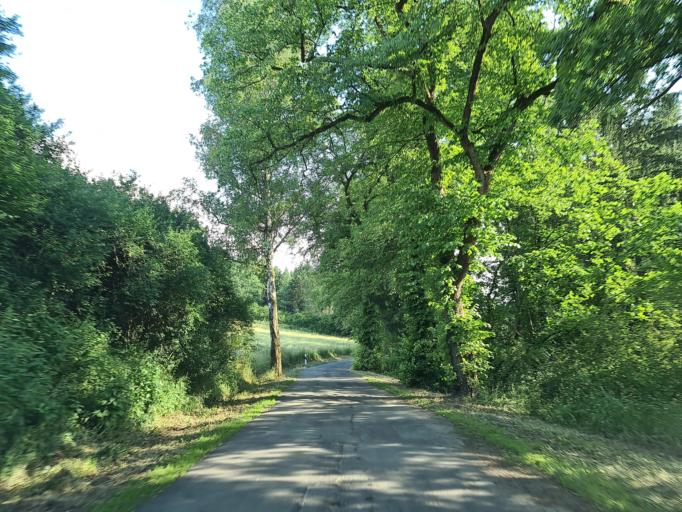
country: DE
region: Saxony
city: Bosenbrunn
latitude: 50.4139
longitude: 12.0946
